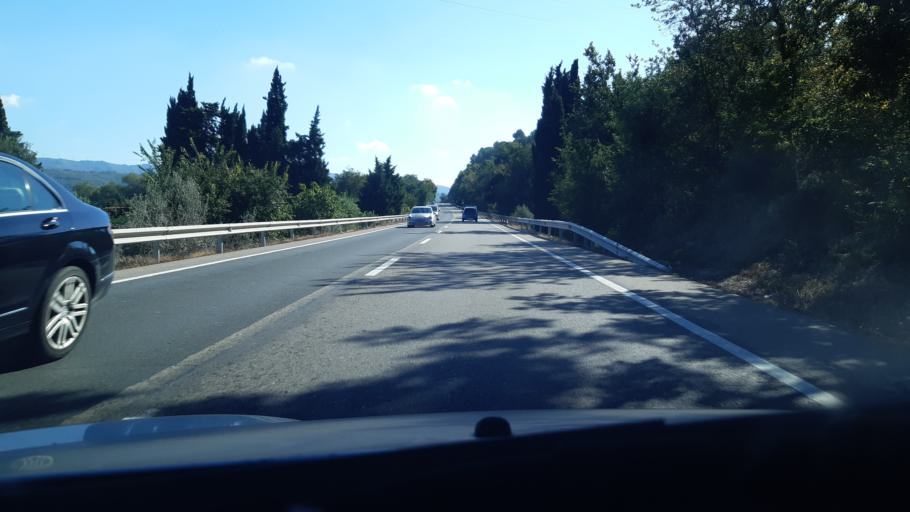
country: ES
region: Catalonia
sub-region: Provincia de Tarragona
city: Tivenys
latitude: 40.8660
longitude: 0.5052
